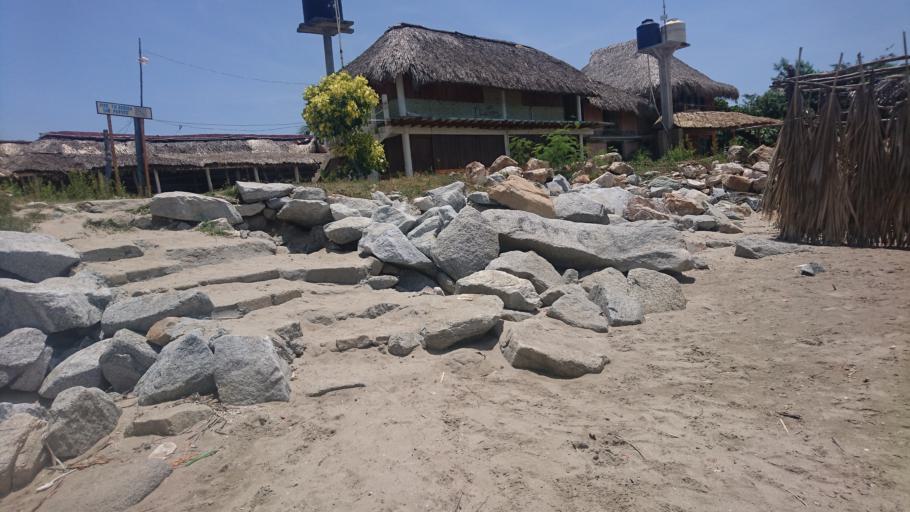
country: MX
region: Oaxaca
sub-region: Villa de Tututepec de Melchor Ocampo
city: Santa Rosa de Lima
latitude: 15.9677
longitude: -97.6776
